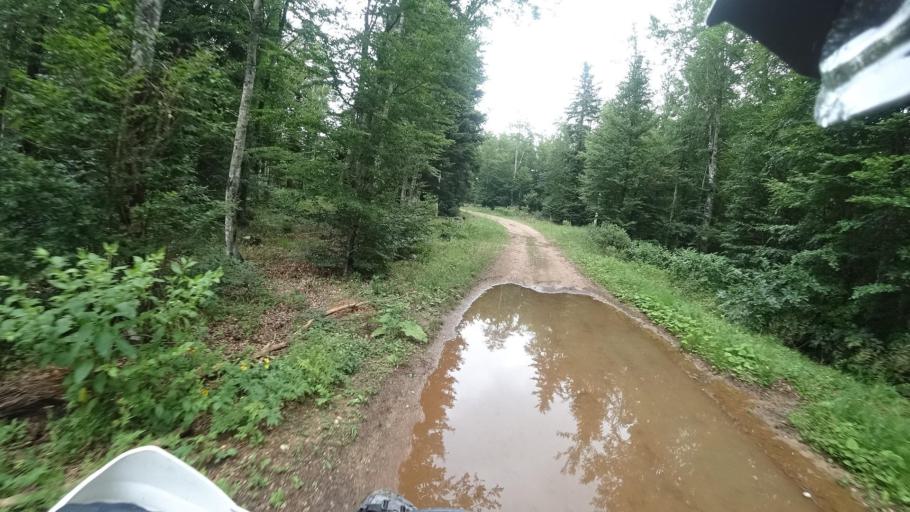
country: BA
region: Federation of Bosnia and Herzegovina
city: Bihac
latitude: 44.6302
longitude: 15.7923
